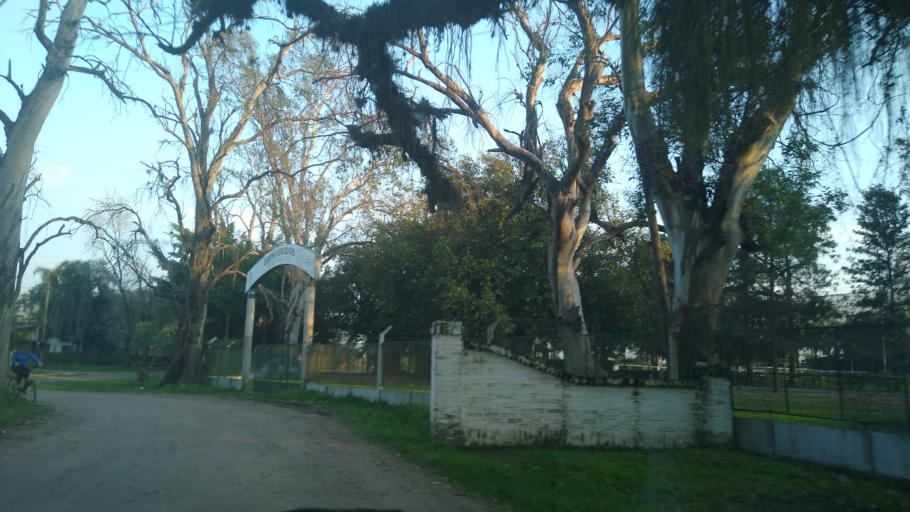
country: AR
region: Chaco
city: Resistencia
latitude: -27.4671
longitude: -58.9577
